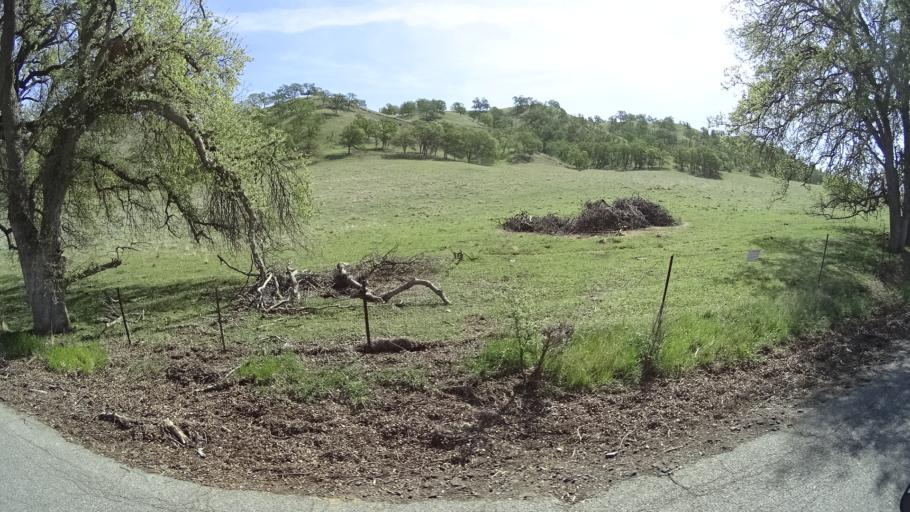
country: US
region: California
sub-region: Glenn County
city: Willows
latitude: 39.5454
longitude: -122.4404
